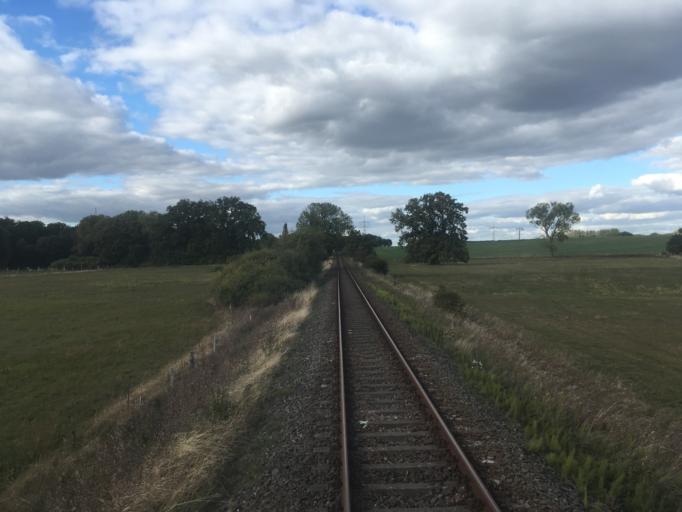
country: DE
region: Mecklenburg-Vorpommern
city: Malchow
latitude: 53.5018
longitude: 12.4286
